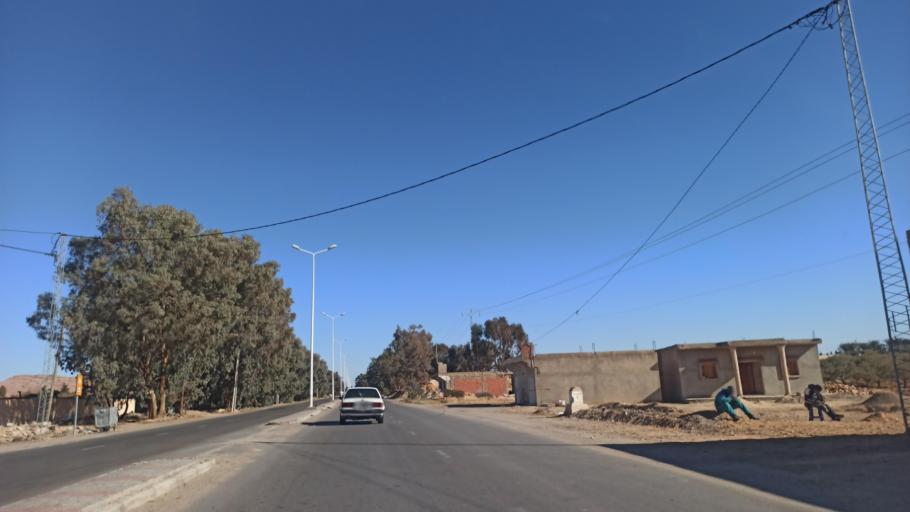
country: TN
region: Gafsa
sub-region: Gafsa Municipality
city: Gafsa
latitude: 34.4035
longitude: 8.7279
